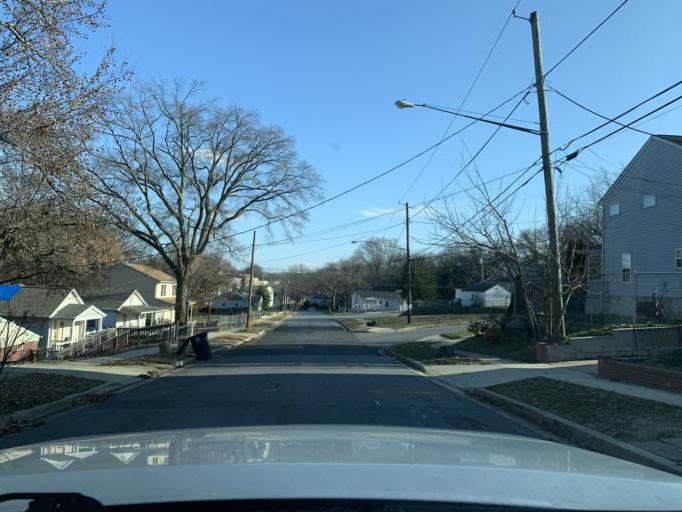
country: US
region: Maryland
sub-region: Prince George's County
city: Fairmount Heights
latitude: 38.9066
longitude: -76.9242
